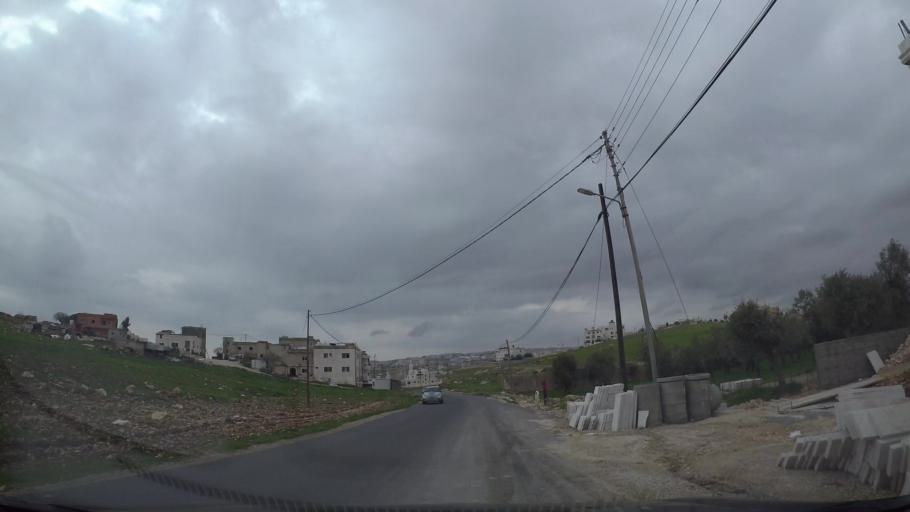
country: JO
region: Amman
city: Wadi as Sir
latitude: 31.9297
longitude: 35.8539
